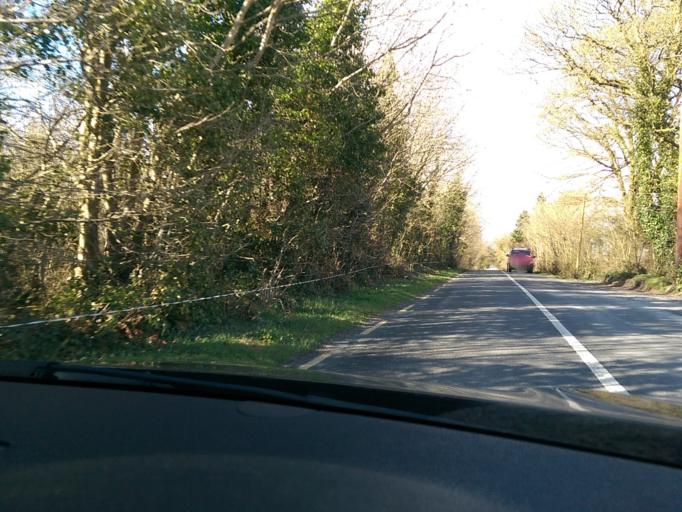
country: IE
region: Connaught
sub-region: Roscommon
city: Castlerea
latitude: 53.5358
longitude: -8.5557
